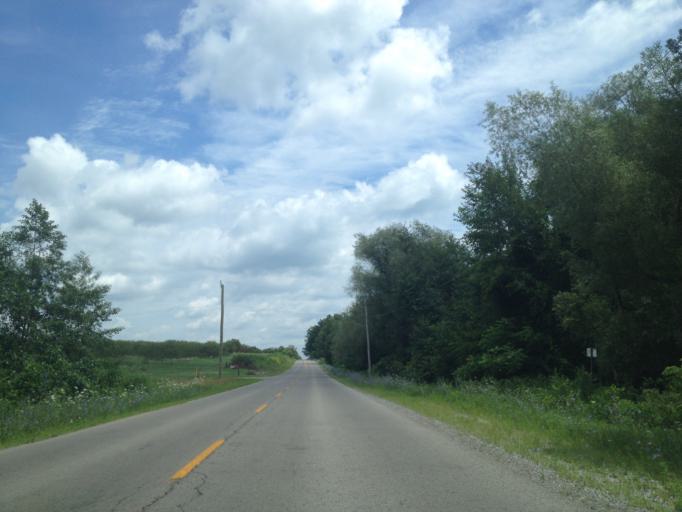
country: CA
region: Ontario
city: Norfolk County
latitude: 42.7746
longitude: -80.2737
